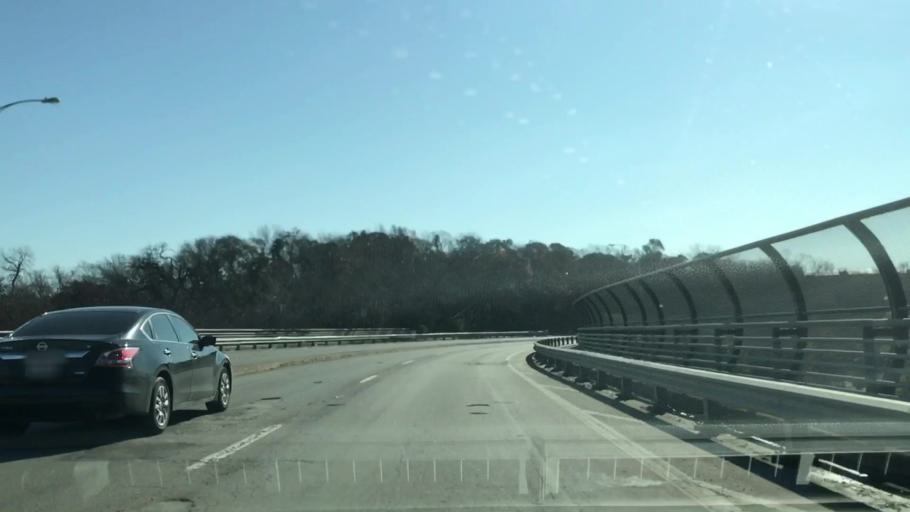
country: US
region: Texas
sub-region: Dallas County
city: Dallas
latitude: 32.7399
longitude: -96.8137
